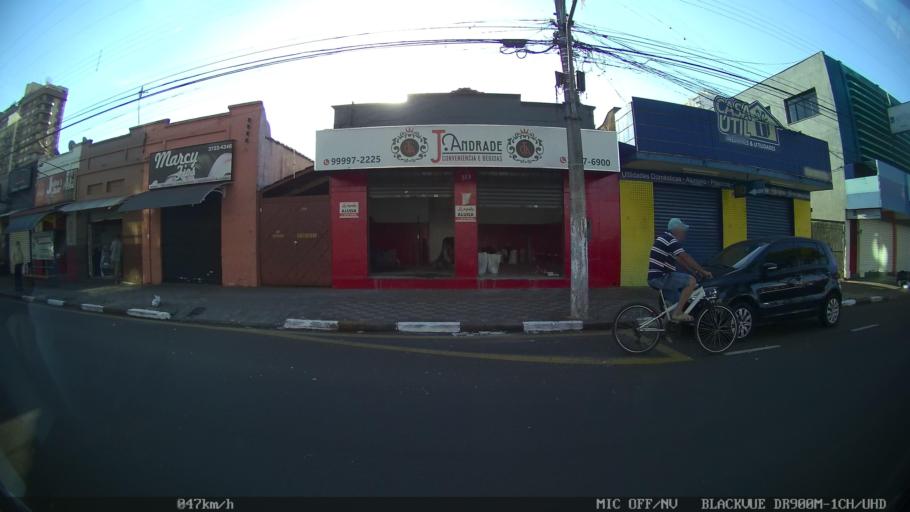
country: BR
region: Sao Paulo
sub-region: Franca
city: Franca
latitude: -20.5312
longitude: -47.3955
